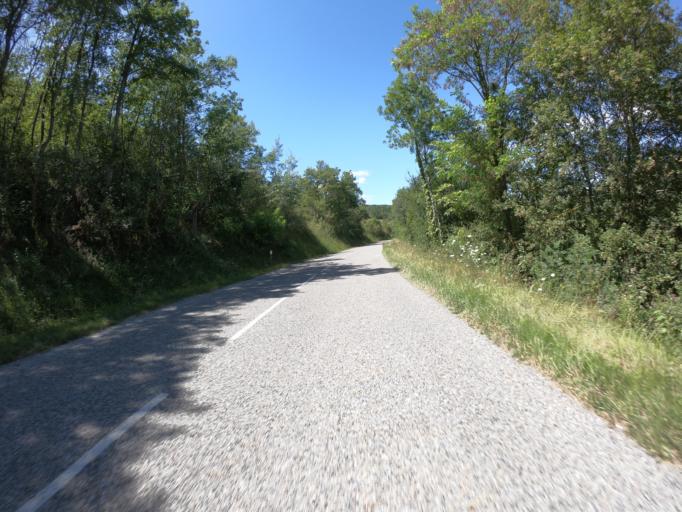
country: FR
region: Midi-Pyrenees
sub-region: Departement de l'Ariege
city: Mirepoix
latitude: 43.0446
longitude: 1.7672
